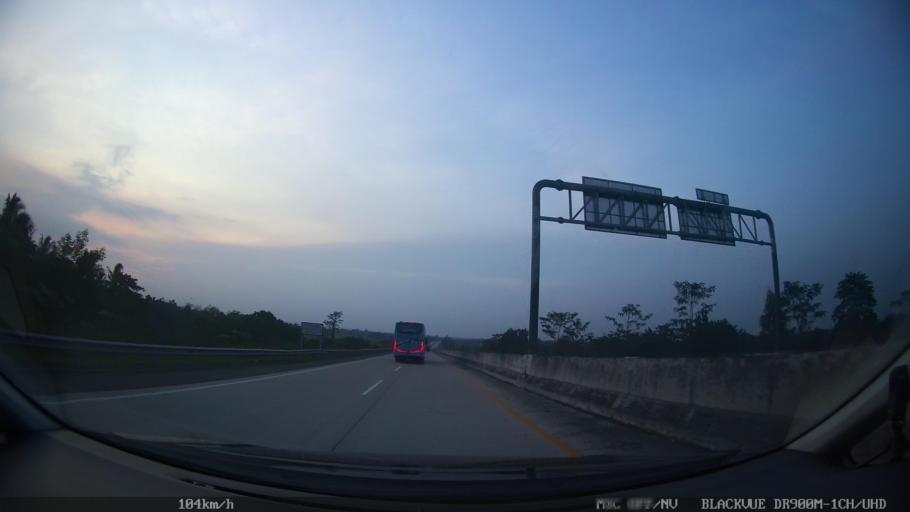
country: ID
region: Lampung
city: Kalianda
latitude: -5.6838
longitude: 105.6131
